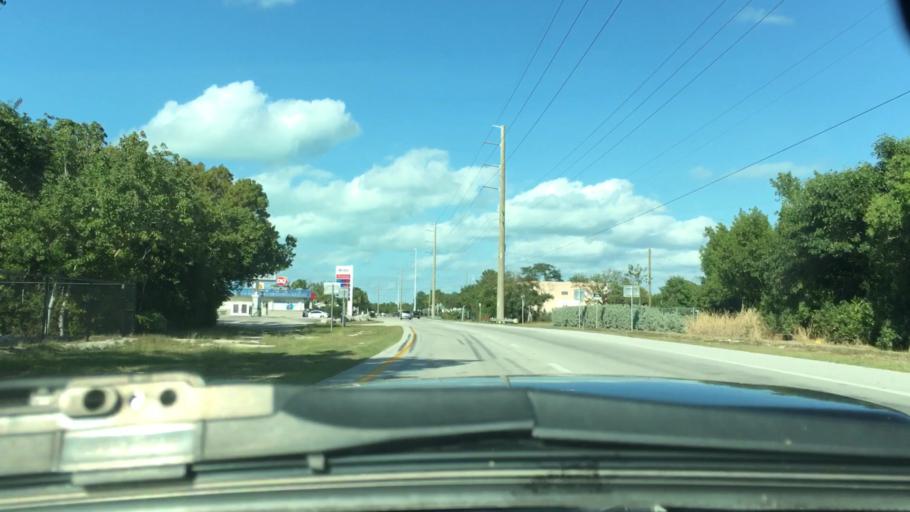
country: US
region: Florida
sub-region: Monroe County
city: Tavernier
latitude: 25.0153
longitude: -80.5117
